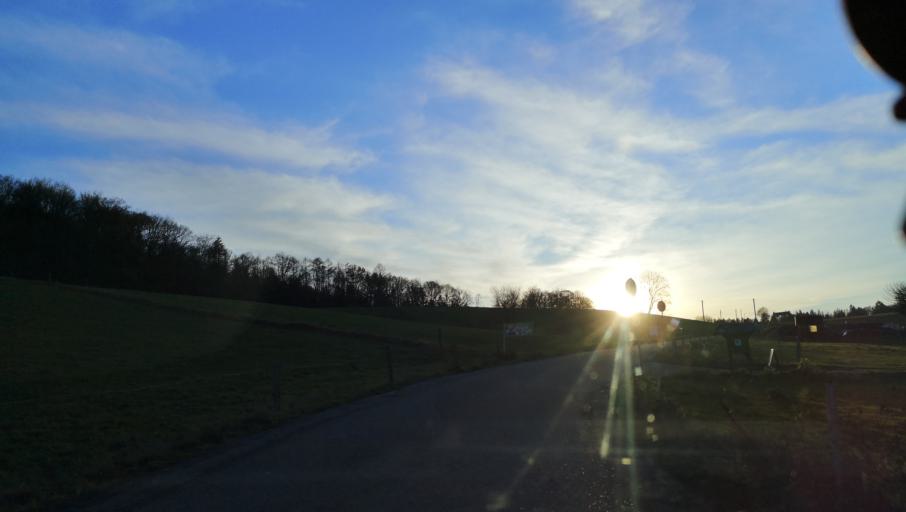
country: DE
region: North Rhine-Westphalia
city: Radevormwald
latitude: 51.1690
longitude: 7.3949
